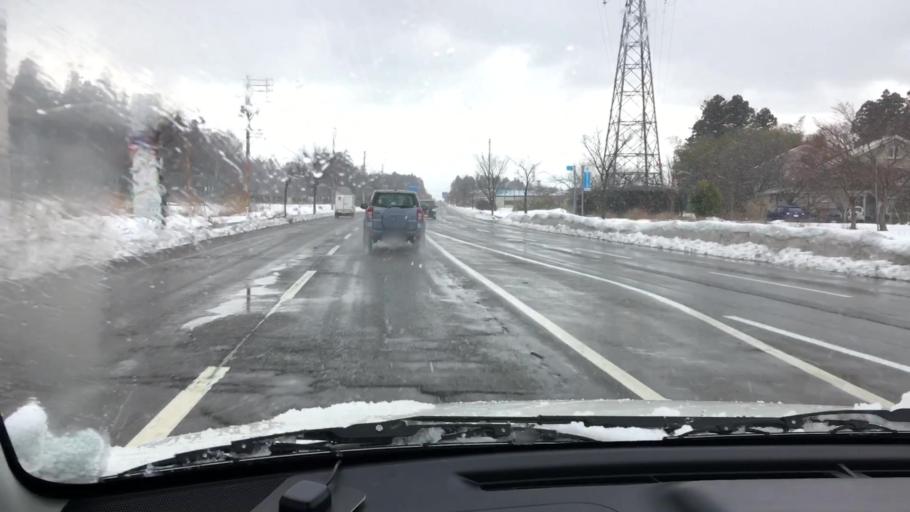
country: JP
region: Niigata
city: Joetsu
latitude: 37.0988
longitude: 138.2309
